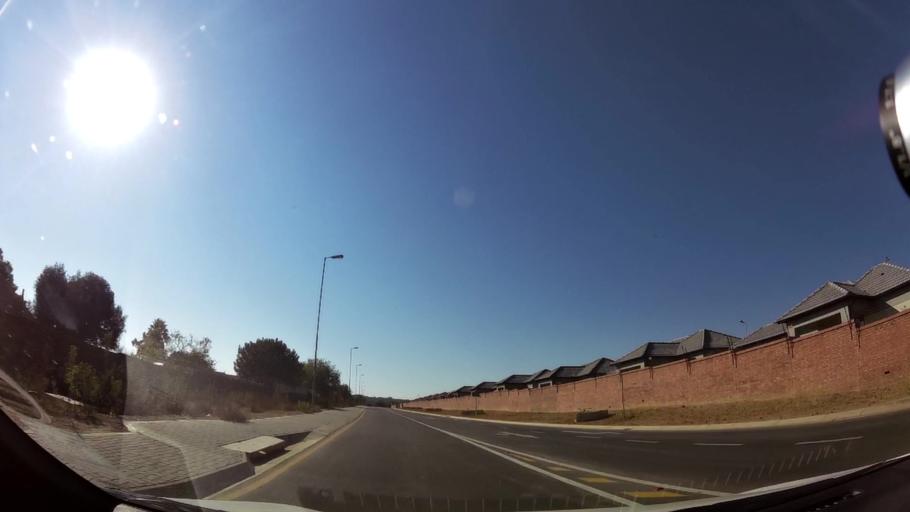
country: ZA
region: Gauteng
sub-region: City of Tshwane Metropolitan Municipality
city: Centurion
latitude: -25.9065
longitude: 28.1256
